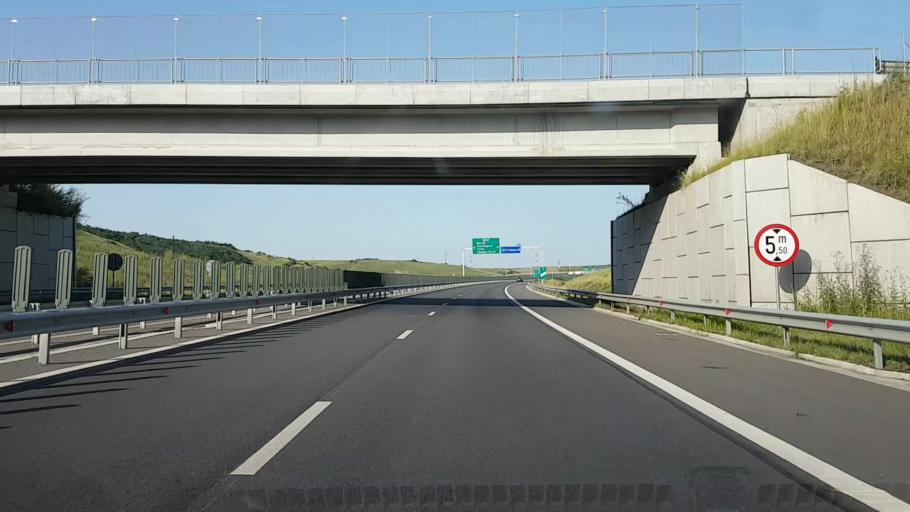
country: RO
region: Alba
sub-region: Comuna Miraslau
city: Miraslau
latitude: 46.3851
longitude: 23.7609
